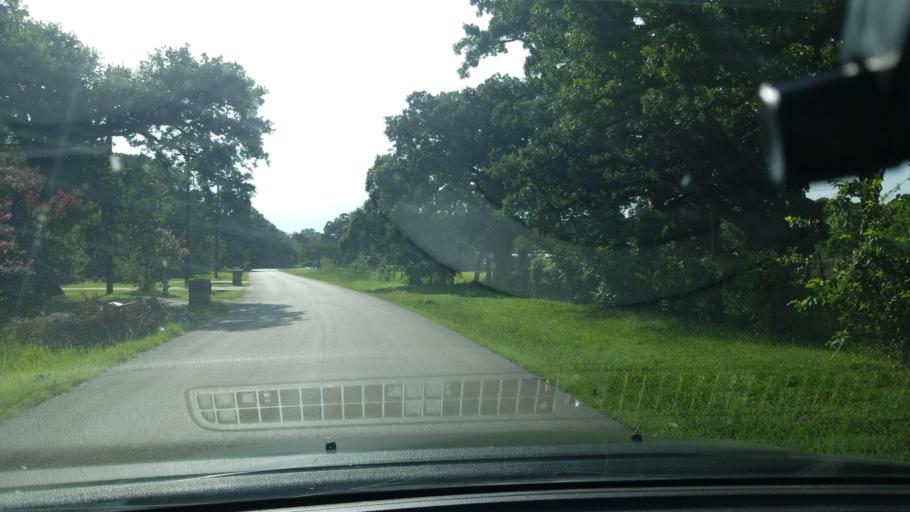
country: US
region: Texas
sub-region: Dallas County
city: Balch Springs
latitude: 32.7151
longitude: -96.6425
